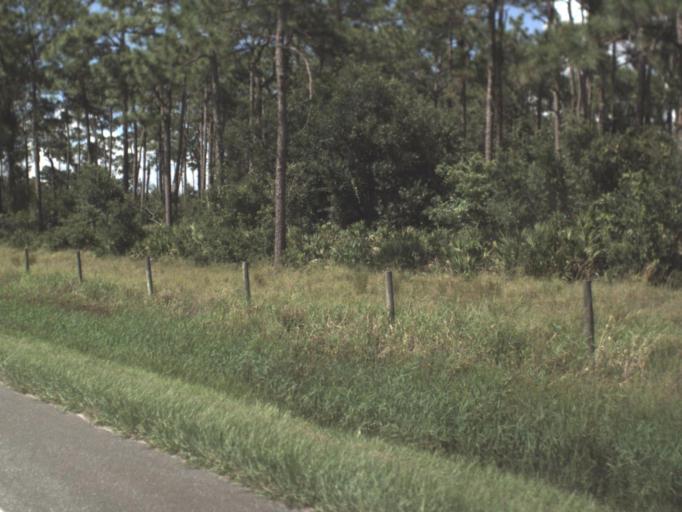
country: US
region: Florida
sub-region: Sarasota County
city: Lake Sarasota
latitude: 27.3745
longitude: -82.2244
